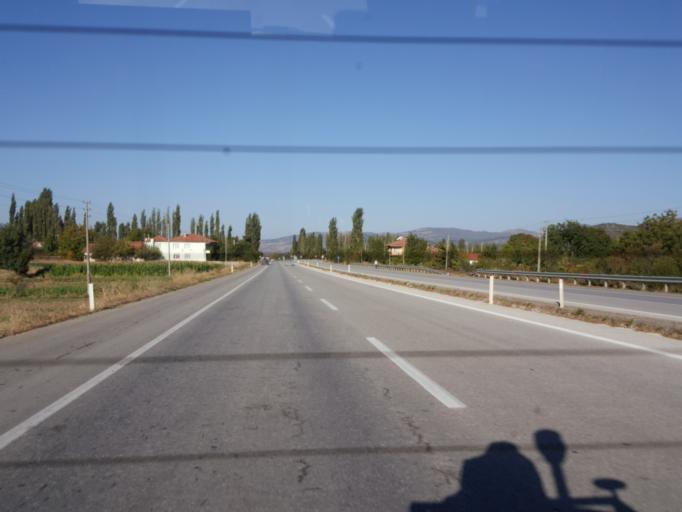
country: TR
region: Amasya
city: Ezinepazari
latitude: 40.5717
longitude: 36.1256
